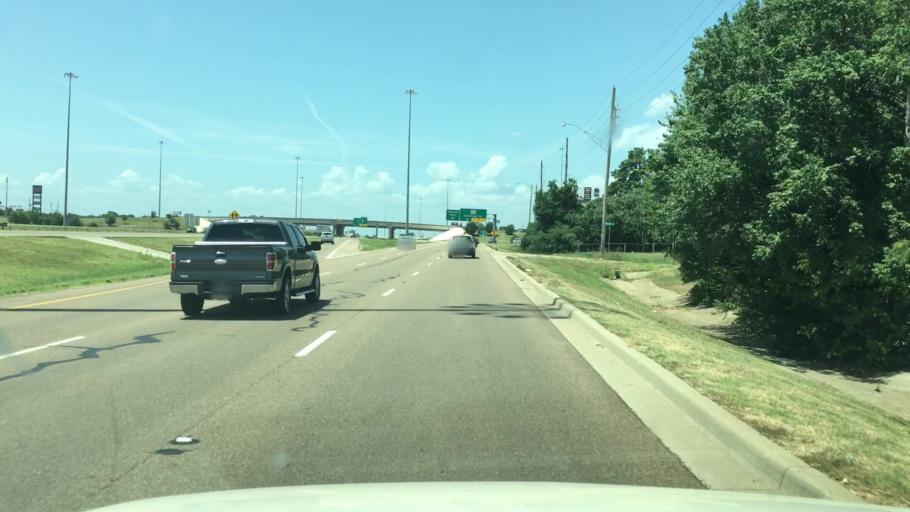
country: US
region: Texas
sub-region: Bowie County
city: Wake Village
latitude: 33.4588
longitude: -94.0824
